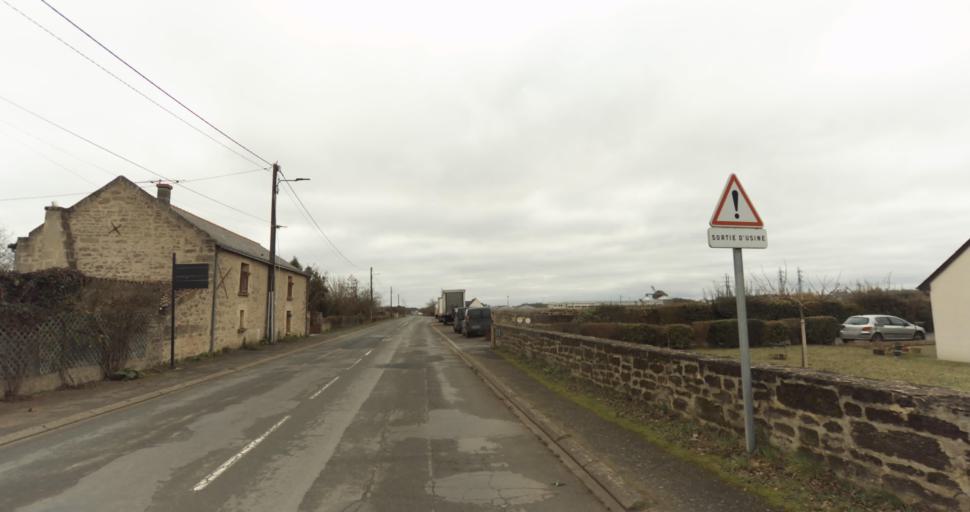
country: FR
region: Pays de la Loire
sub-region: Departement de Maine-et-Loire
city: Doue-la-Fontaine
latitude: 47.1856
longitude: -0.2548
